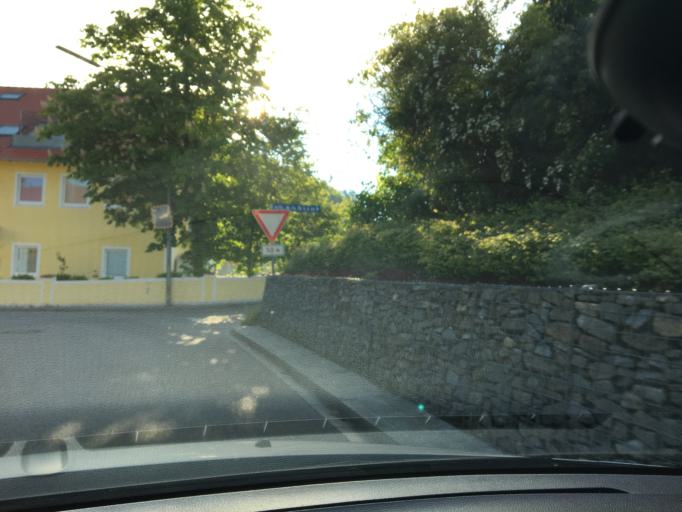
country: DE
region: Bavaria
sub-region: Lower Bavaria
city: Stallwang
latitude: 48.5323
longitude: 12.2357
